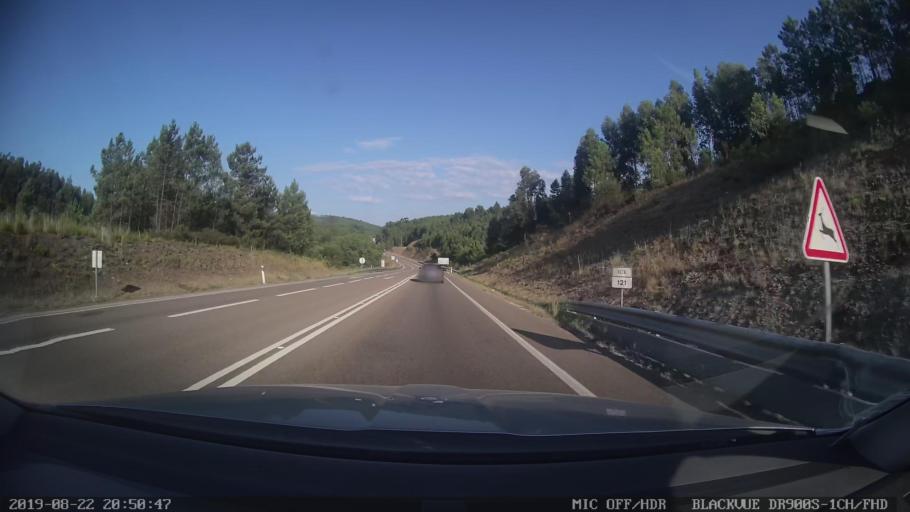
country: PT
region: Castelo Branco
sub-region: Proenca-A-Nova
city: Proenca-a-Nova
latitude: 39.7572
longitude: -7.9458
